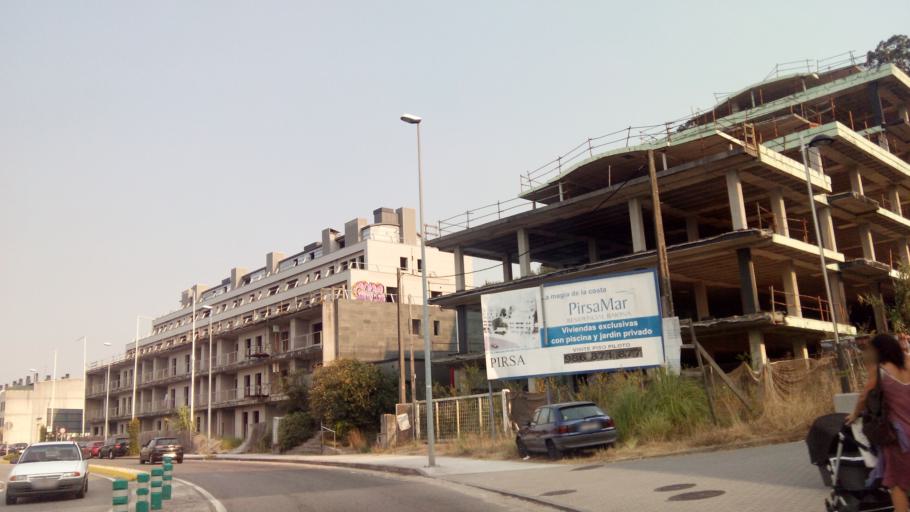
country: ES
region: Galicia
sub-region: Provincia de Pontevedra
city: Baiona
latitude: 42.1110
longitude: -8.8350
